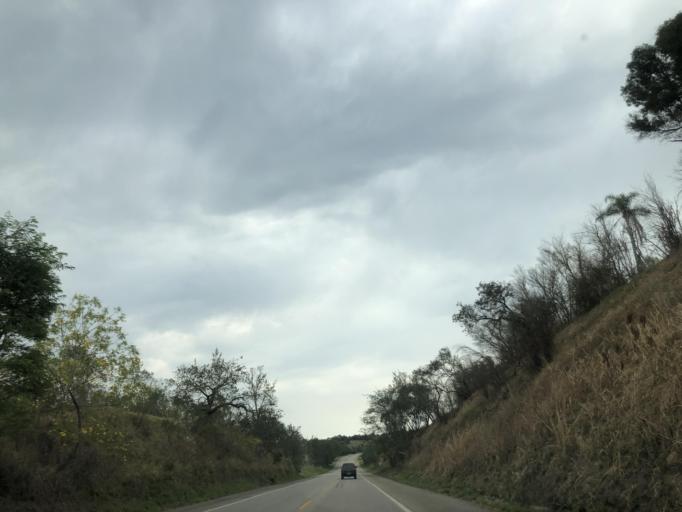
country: BR
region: Sao Paulo
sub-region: Salto De Pirapora
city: Salto de Pirapora
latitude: -23.7179
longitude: -47.6383
